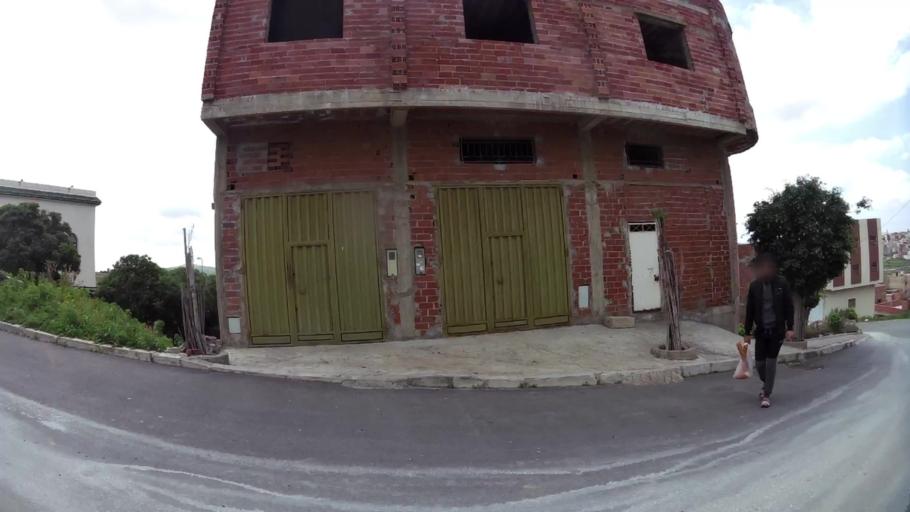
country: MA
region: Tanger-Tetouan
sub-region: Tanger-Assilah
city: Tangier
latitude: 35.7686
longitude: -5.7501
